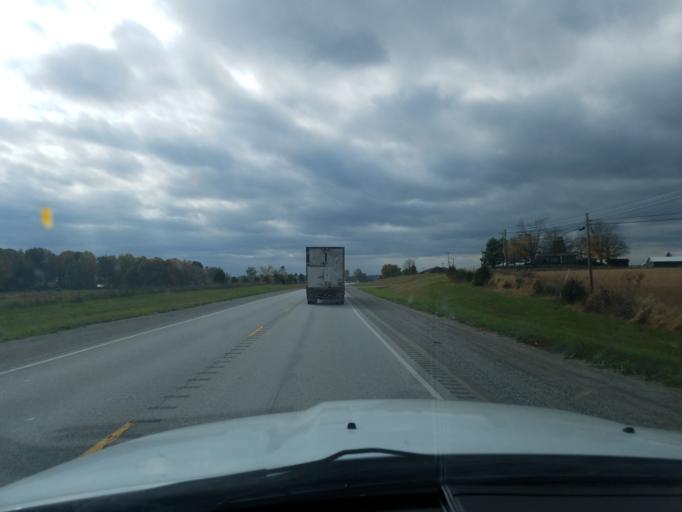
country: US
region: Kentucky
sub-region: Taylor County
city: Campbellsville
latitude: 37.3669
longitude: -85.3080
